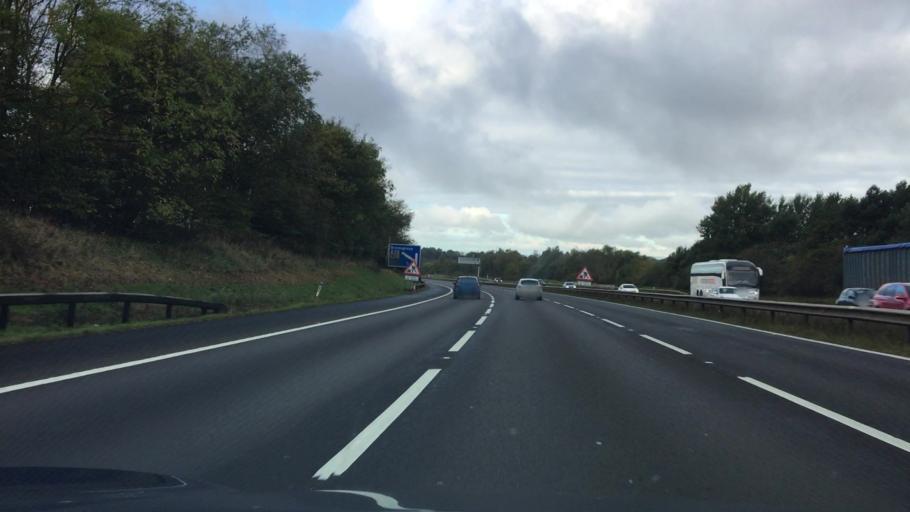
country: GB
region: England
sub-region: Worcestershire
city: Barnt Green
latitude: 52.3570
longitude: -2.0268
